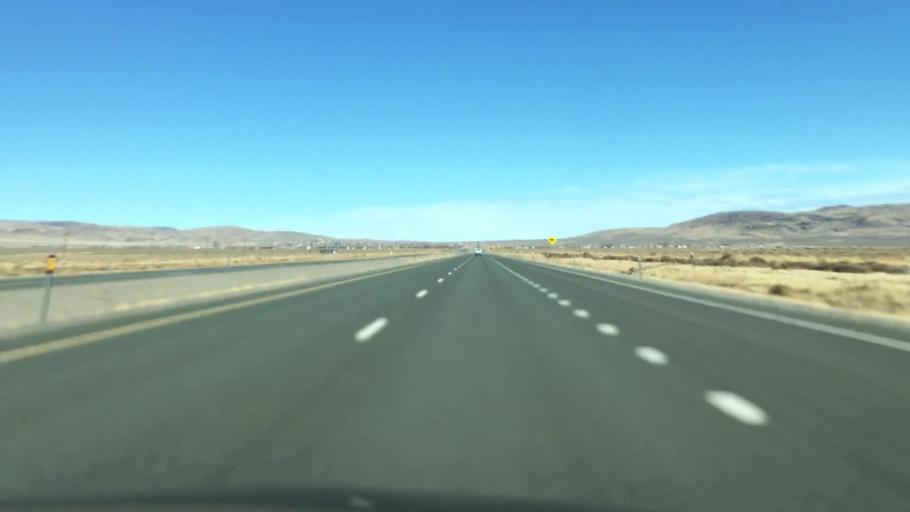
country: US
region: Nevada
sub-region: Lyon County
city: Stagecoach
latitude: 39.3429
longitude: -119.4245
